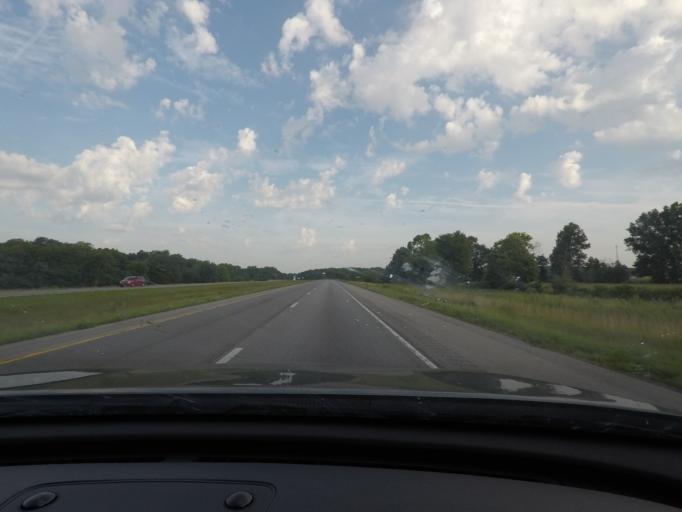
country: US
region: Illinois
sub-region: Clinton County
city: Wamac
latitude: 38.3751
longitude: -89.1018
